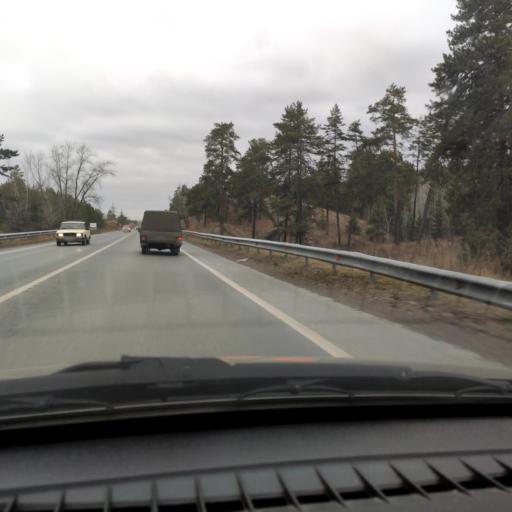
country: RU
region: Samara
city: Volzhskiy
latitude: 53.4450
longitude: 50.1013
